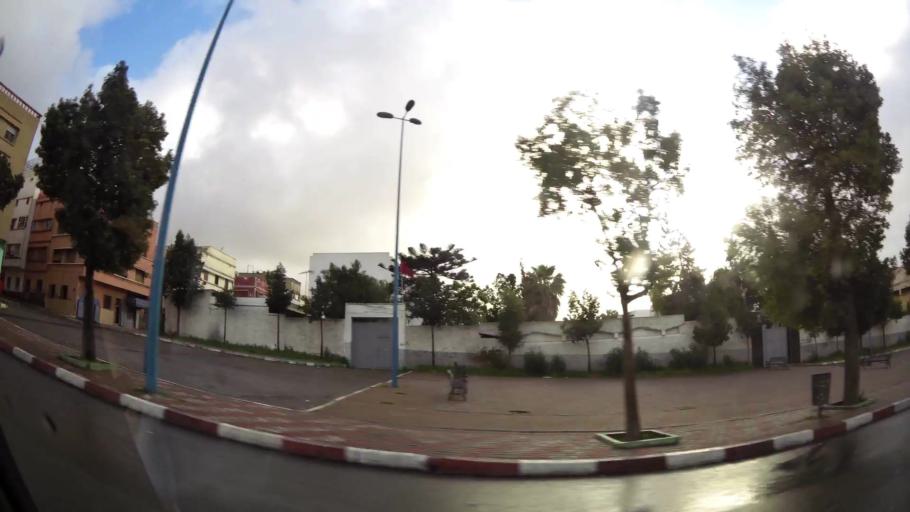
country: MA
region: Grand Casablanca
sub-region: Casablanca
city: Casablanca
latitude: 33.5591
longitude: -7.5747
